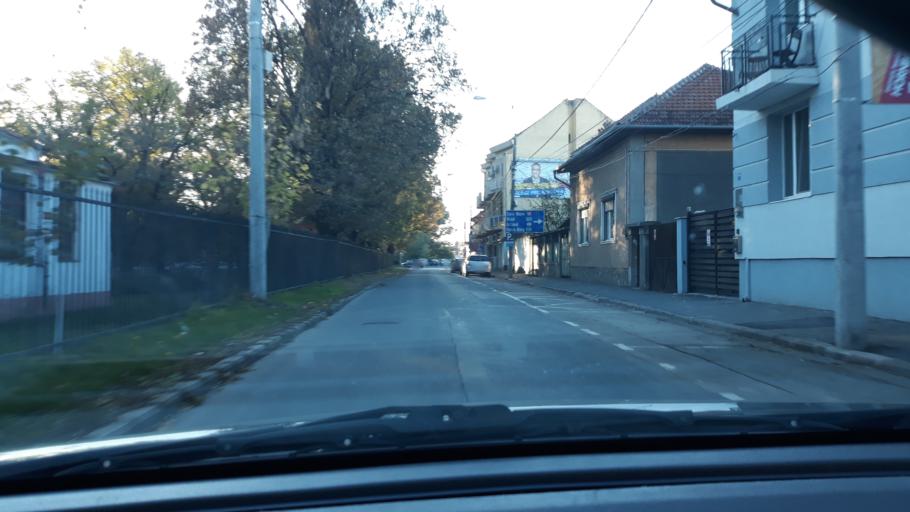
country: RO
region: Bihor
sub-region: Comuna Biharea
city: Oradea
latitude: 47.0511
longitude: 21.9215
